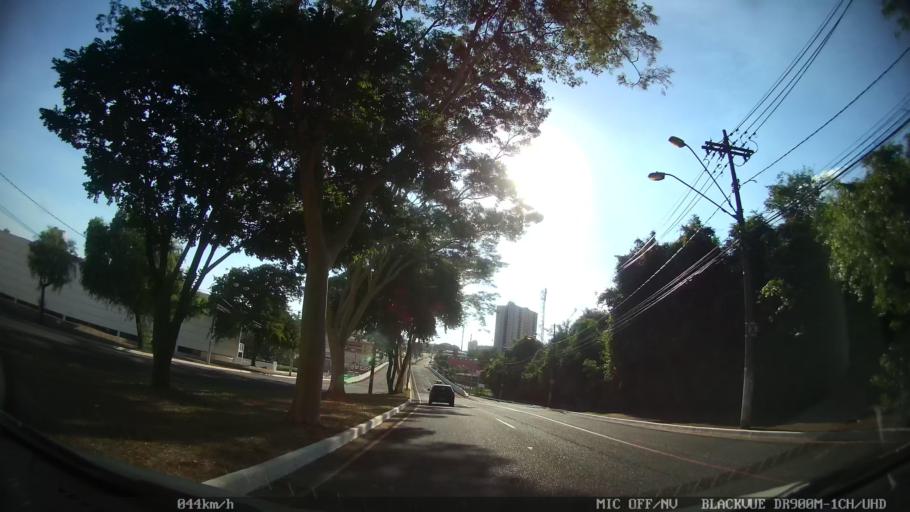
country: BR
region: Sao Paulo
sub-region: Ribeirao Preto
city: Ribeirao Preto
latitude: -21.1955
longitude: -47.7961
